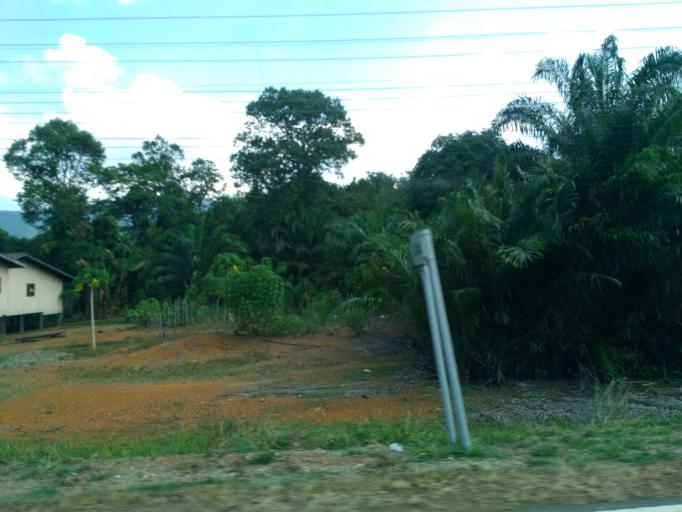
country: MY
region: Sabah
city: Ranau
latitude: 5.6244
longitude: 117.0986
